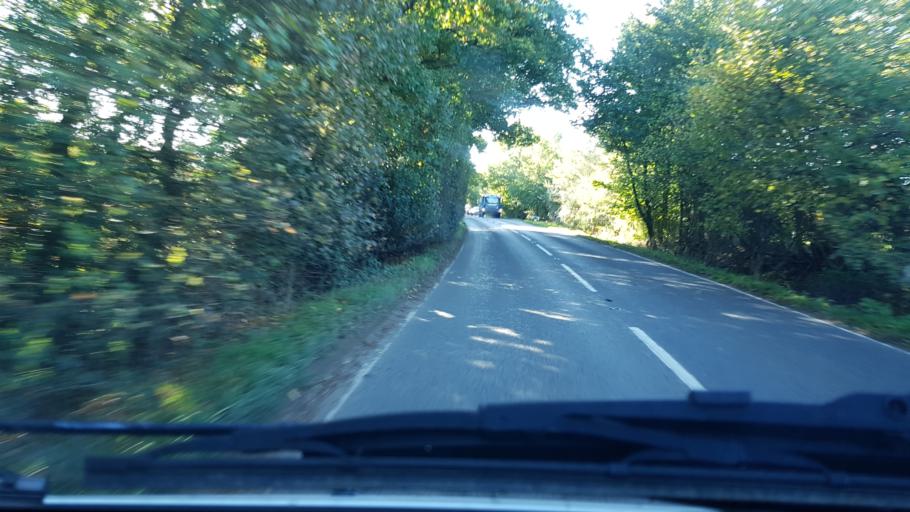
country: GB
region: England
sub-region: Surrey
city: Cranleigh
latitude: 51.1681
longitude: -0.5109
